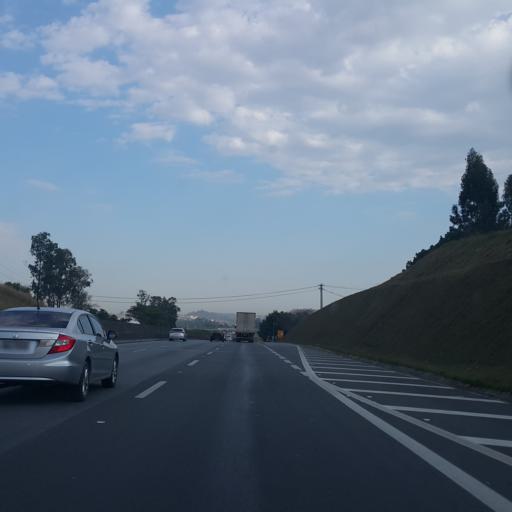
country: BR
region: Sao Paulo
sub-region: Vinhedo
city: Vinhedo
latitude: -23.0686
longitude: -46.9879
